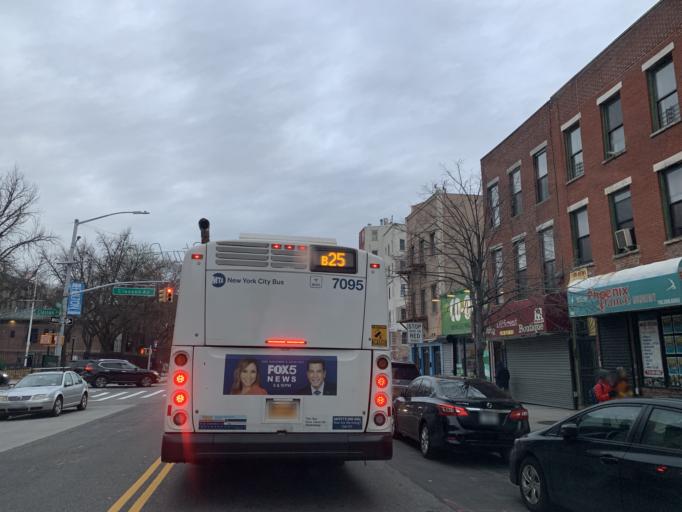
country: US
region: New York
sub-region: Kings County
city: Brooklyn
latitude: 40.6817
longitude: -73.9581
